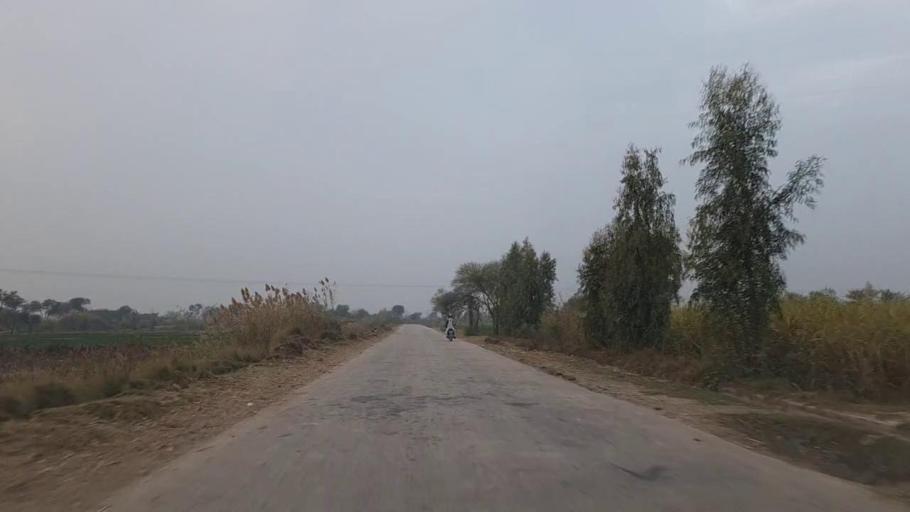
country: PK
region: Sindh
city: Jam Sahib
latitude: 26.3232
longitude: 68.5461
